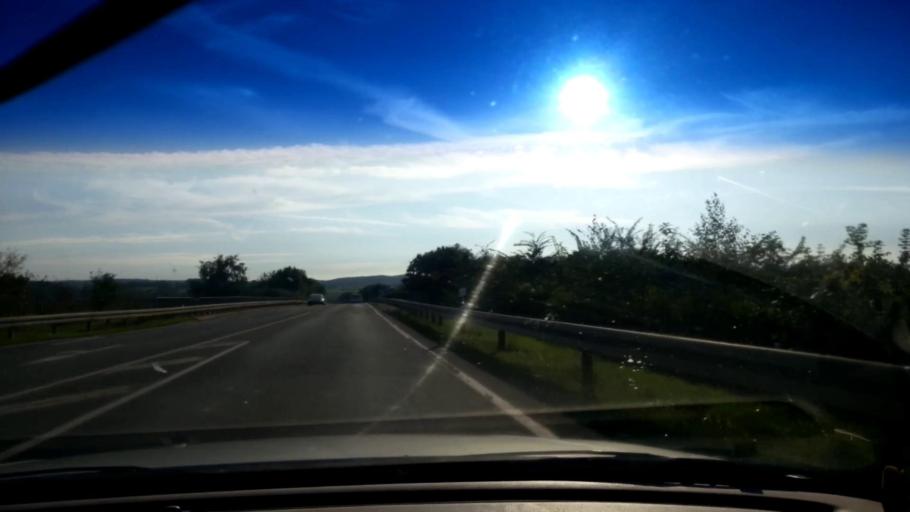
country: DE
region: Bavaria
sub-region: Upper Franconia
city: Viereth-Trunstadt
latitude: 49.9324
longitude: 10.7801
